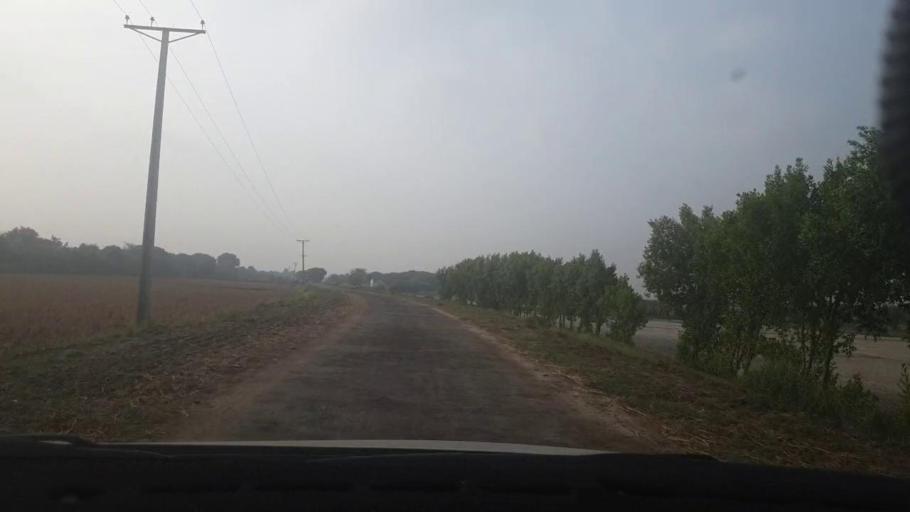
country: PK
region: Sindh
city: Tando Muhammad Khan
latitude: 25.0962
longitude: 68.5163
